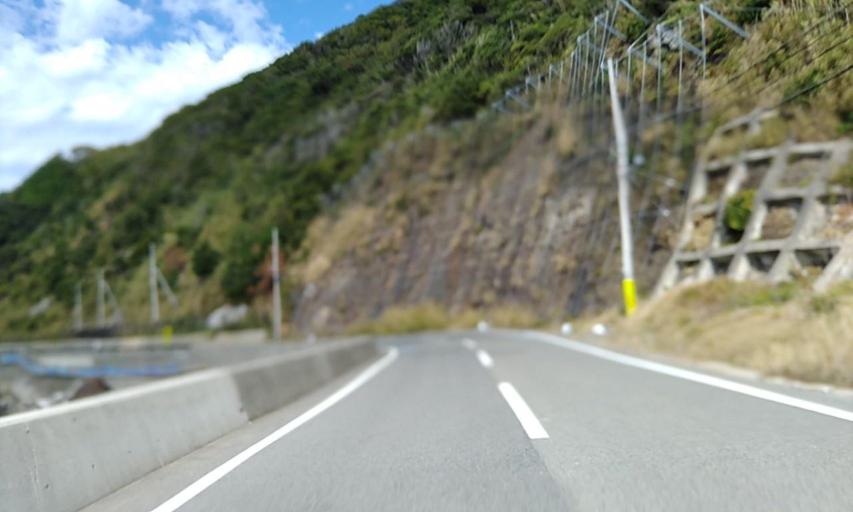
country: JP
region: Wakayama
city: Gobo
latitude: 33.9728
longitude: 135.0787
